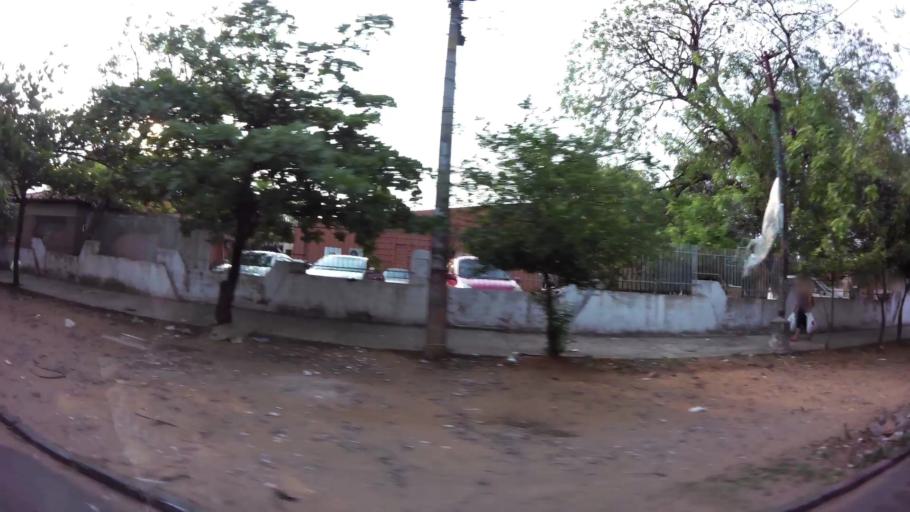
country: PY
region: Central
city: Lambare
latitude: -25.3199
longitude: -57.5772
